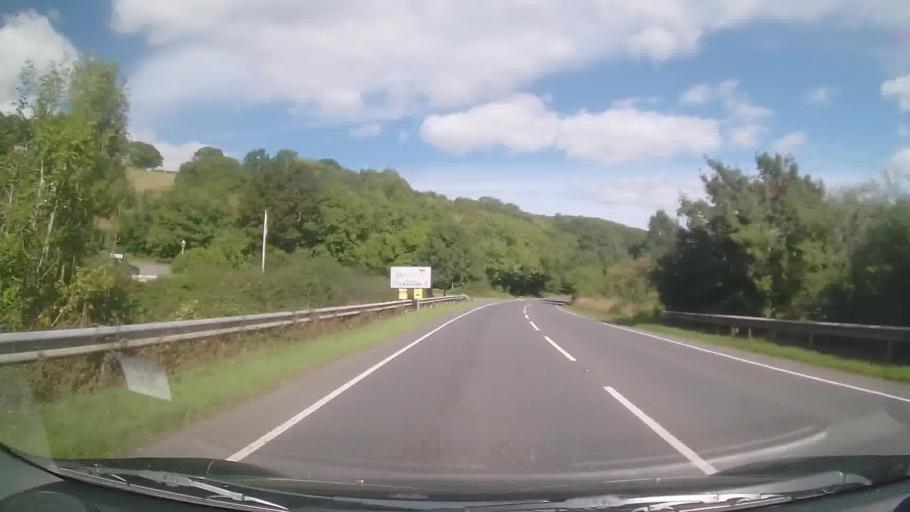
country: GB
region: England
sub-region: Herefordshire
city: Clifford
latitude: 52.1184
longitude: -3.1061
